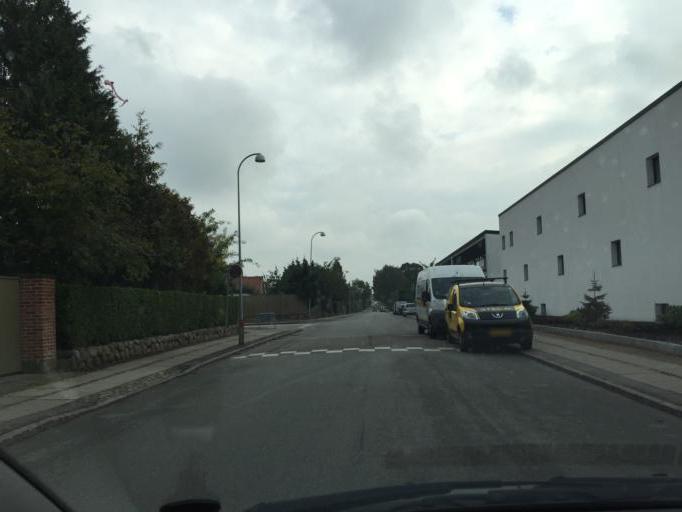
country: DK
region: Capital Region
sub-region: Gladsaxe Municipality
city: Buddinge
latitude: 55.7613
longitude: 12.4731
